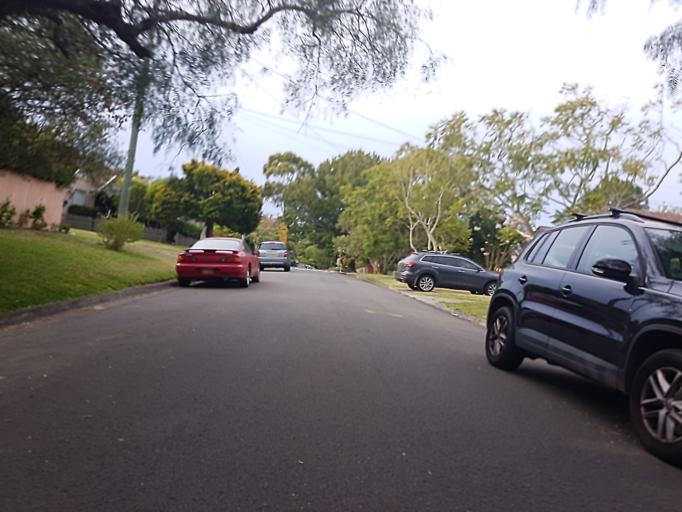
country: AU
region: New South Wales
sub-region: Willoughby
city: Castle Cove
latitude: -33.8001
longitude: 151.2056
